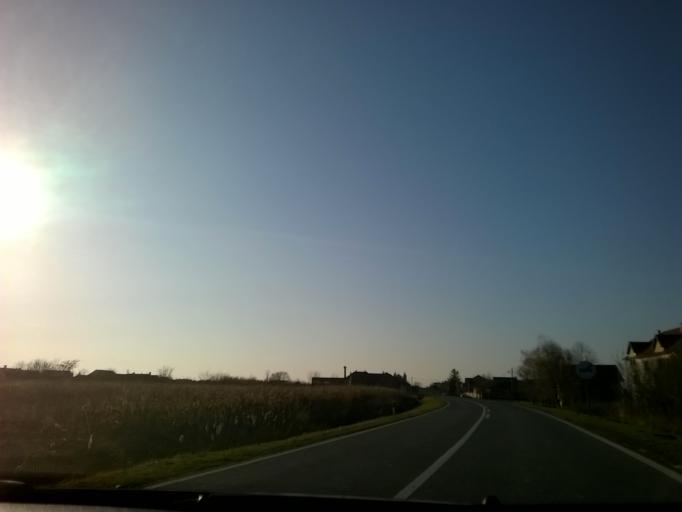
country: RS
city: Nikolinci
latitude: 45.0535
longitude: 21.0798
